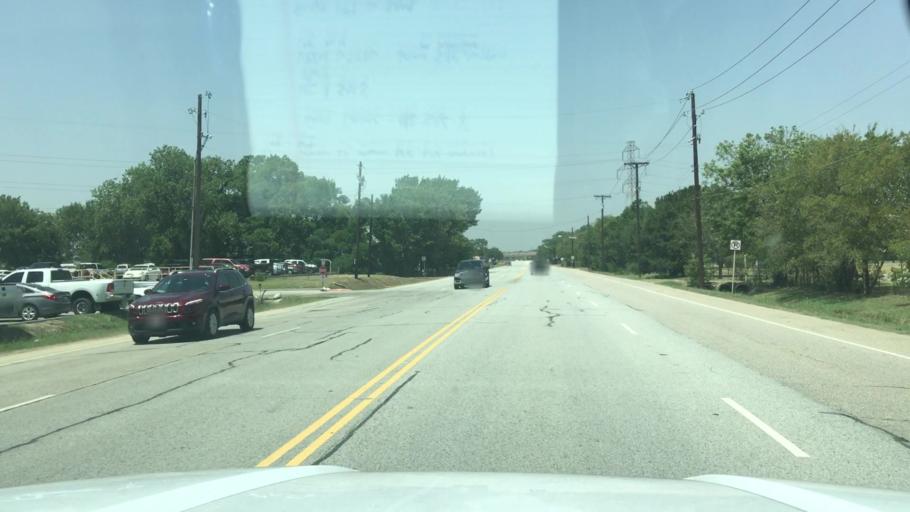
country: US
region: Texas
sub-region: Dallas County
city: Carrollton
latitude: 32.9686
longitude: -96.9233
